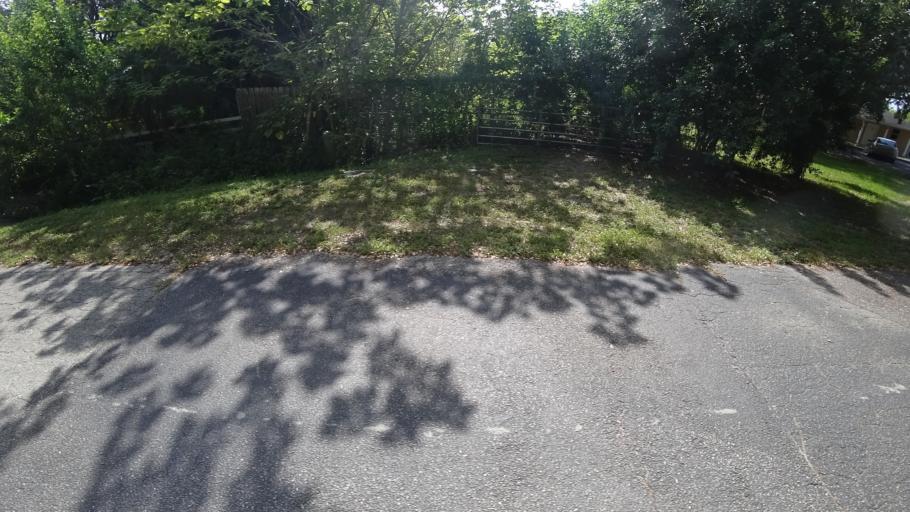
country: US
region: Florida
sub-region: Manatee County
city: Samoset
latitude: 27.4401
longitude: -82.5342
